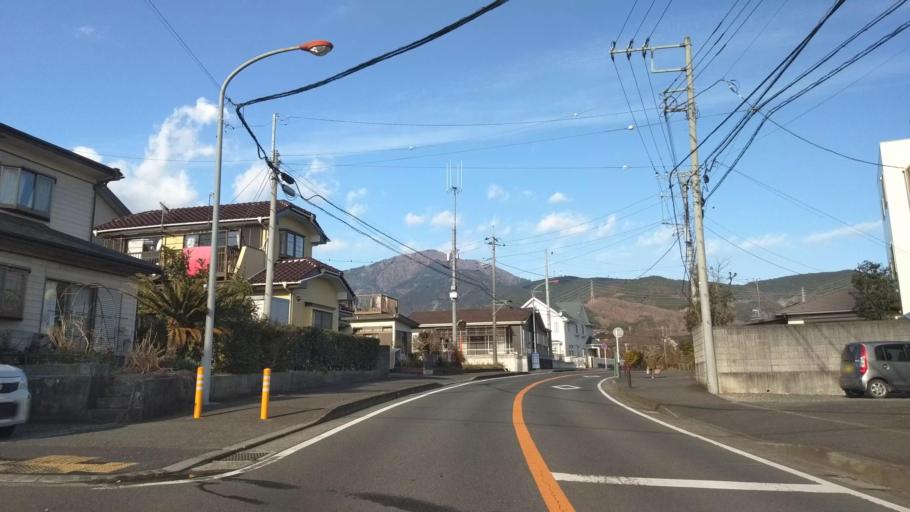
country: JP
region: Kanagawa
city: Hadano
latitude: 35.3907
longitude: 139.2347
